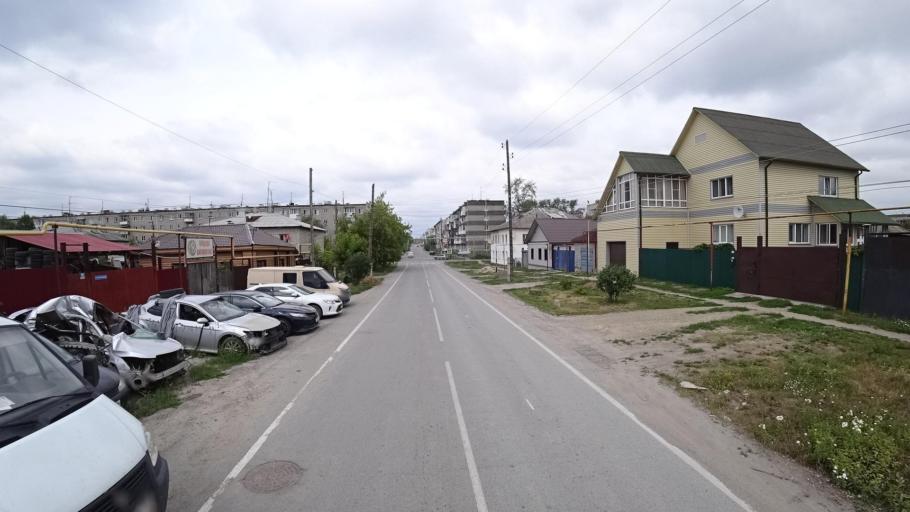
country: RU
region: Sverdlovsk
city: Kamyshlov
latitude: 56.8382
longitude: 62.7167
